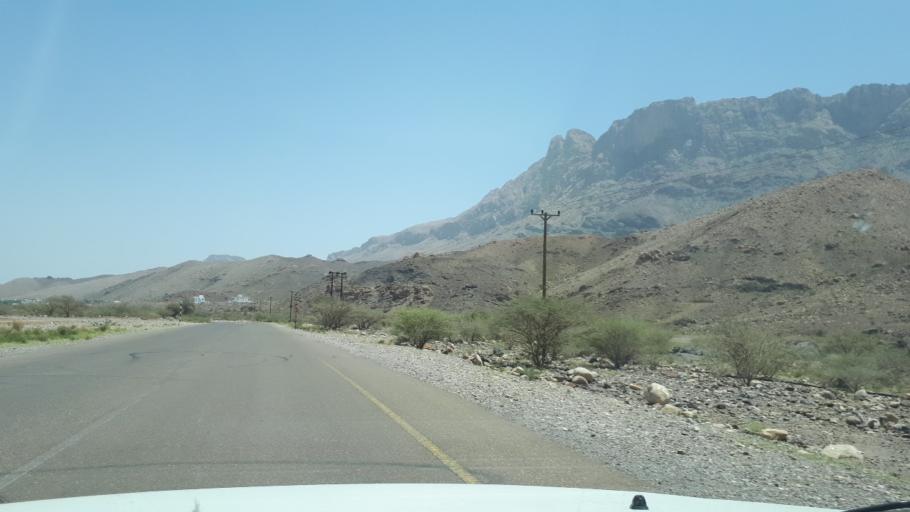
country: OM
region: Muhafazat ad Dakhiliyah
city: Bahla'
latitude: 23.1607
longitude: 57.1673
